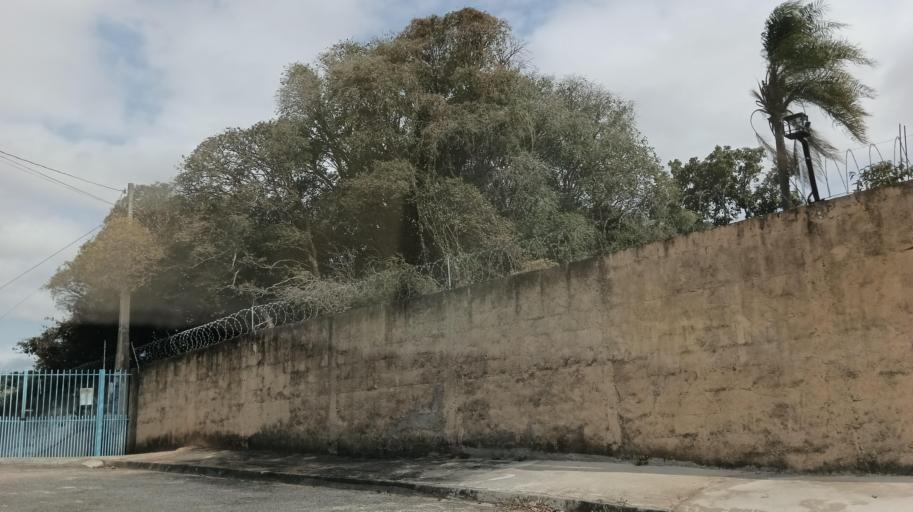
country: BR
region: Sao Paulo
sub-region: Sorocaba
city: Sorocaba
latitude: -23.4768
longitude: -47.4562
